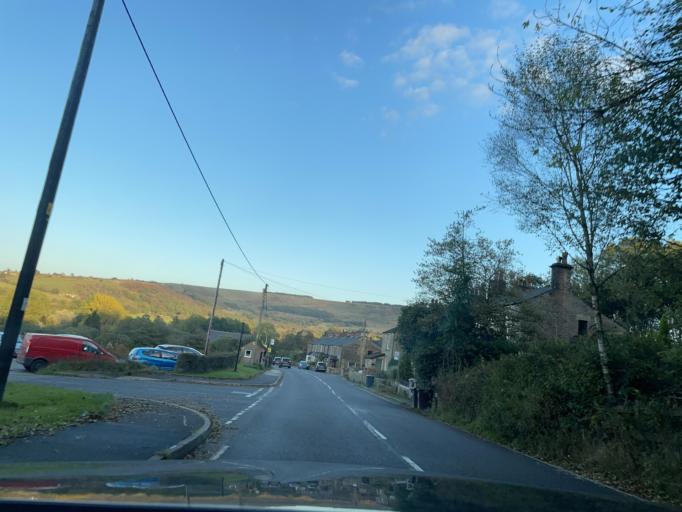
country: GB
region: England
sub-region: Borough of Tameside
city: Longdendale
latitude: 53.4264
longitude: -2.0063
